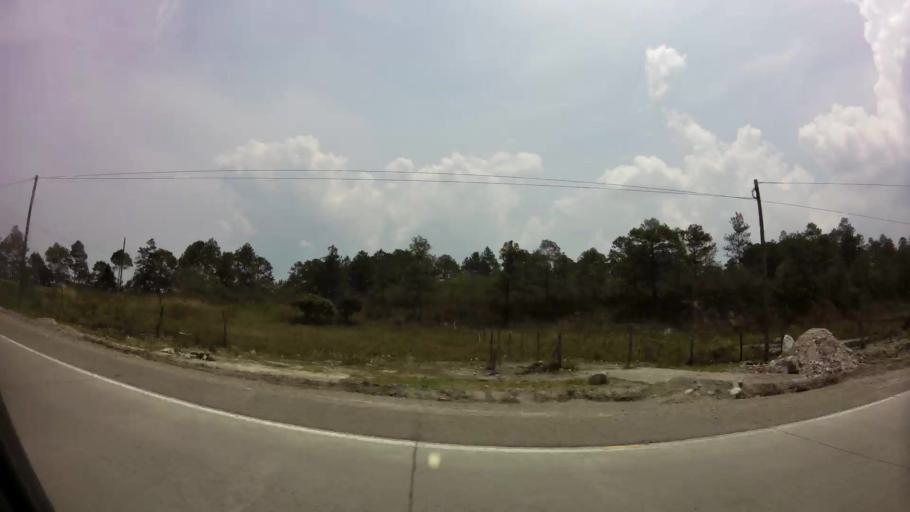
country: HN
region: Comayagua
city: El Socorro
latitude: 14.6461
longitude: -87.9272
